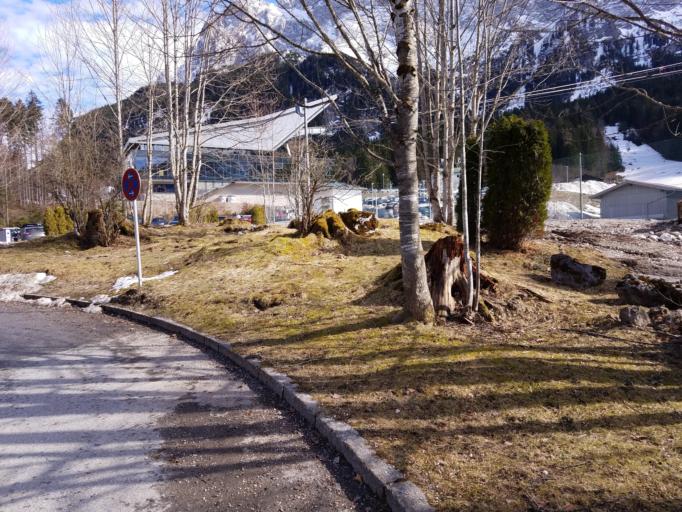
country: DE
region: Bavaria
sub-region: Upper Bavaria
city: Grainau
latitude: 47.4570
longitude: 10.9907
